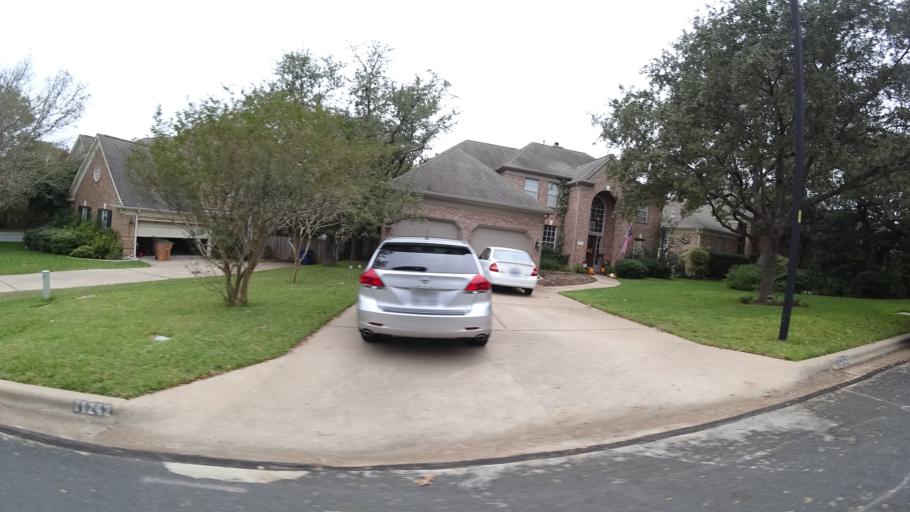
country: US
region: Texas
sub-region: Travis County
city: Shady Hollow
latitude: 30.1856
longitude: -97.8969
